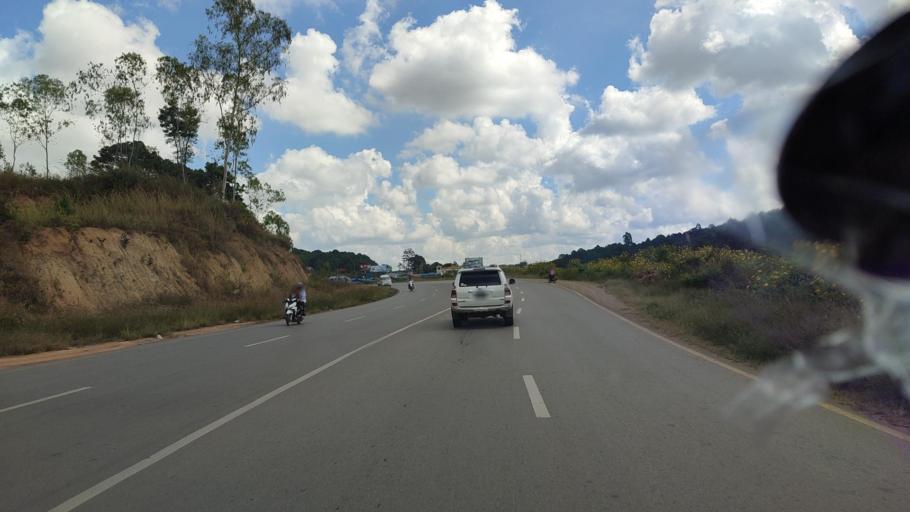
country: MM
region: Shan
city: Taunggyi
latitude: 20.6490
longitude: 96.6179
